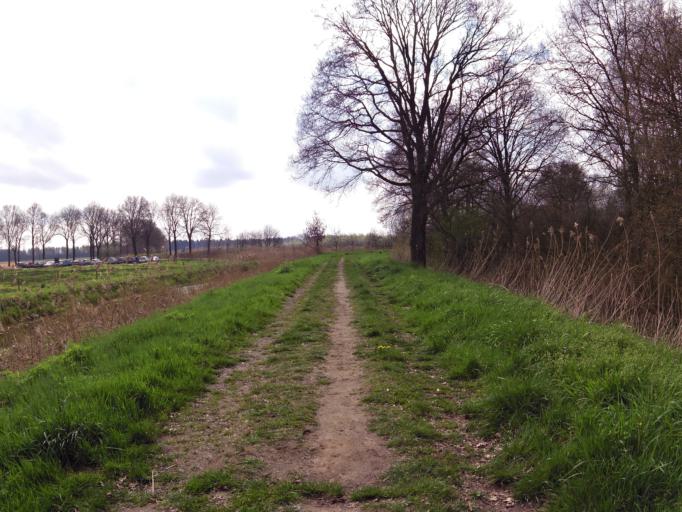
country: NL
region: North Brabant
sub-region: Gemeente Oirschot
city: Oirschot
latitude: 51.5442
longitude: 5.2688
